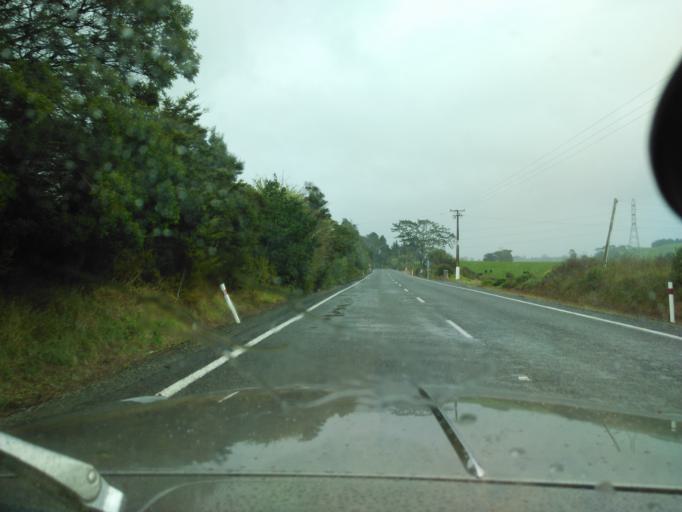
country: NZ
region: Auckland
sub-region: Auckland
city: Wellsford
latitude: -36.3248
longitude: 174.4775
